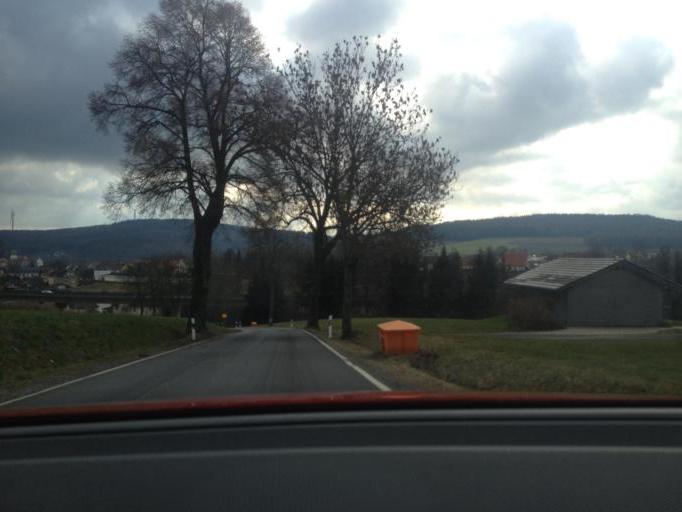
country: DE
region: Bavaria
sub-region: Upper Franconia
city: Arzberg
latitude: 50.0596
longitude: 12.1709
